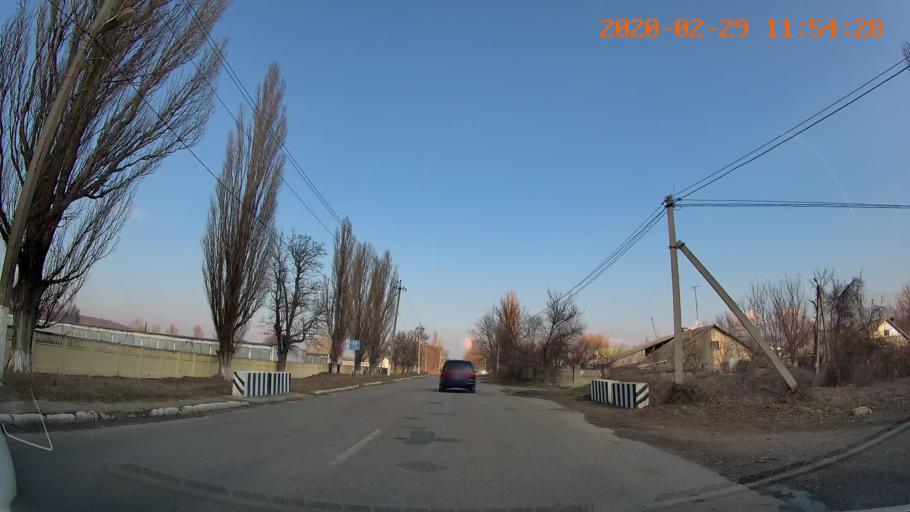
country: MD
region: Telenesti
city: Ribnita
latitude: 47.7846
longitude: 28.9952
